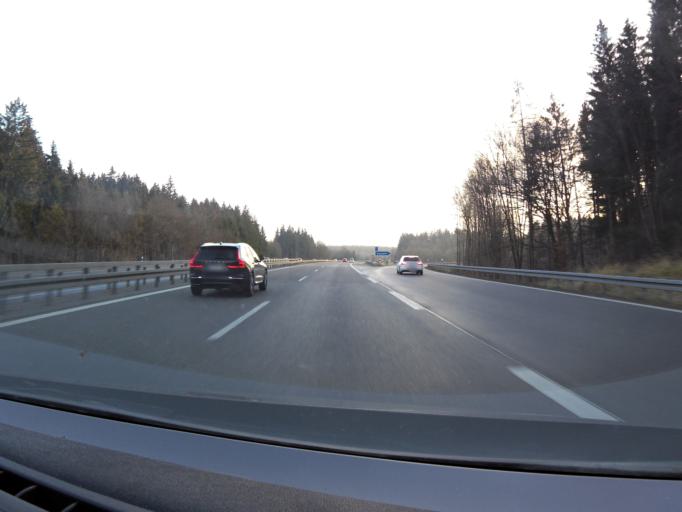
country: DE
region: Bavaria
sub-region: Upper Bavaria
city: Wolfratshausen
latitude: 47.9063
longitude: 11.3959
